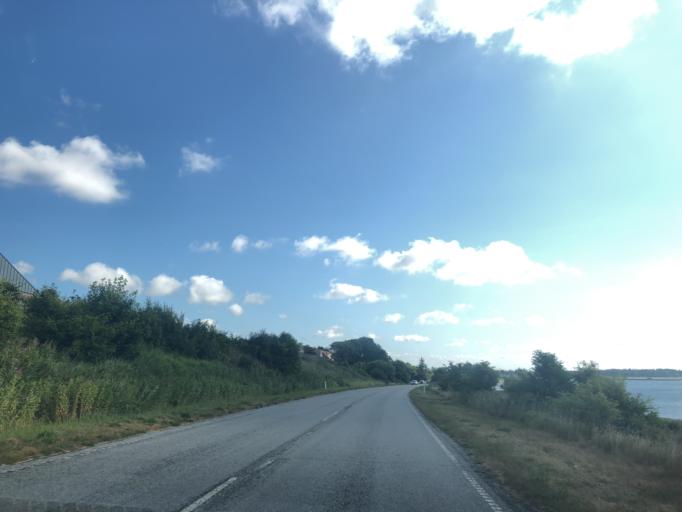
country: DK
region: North Denmark
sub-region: Morso Kommune
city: Nykobing Mors
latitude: 57.0018
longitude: 8.9271
